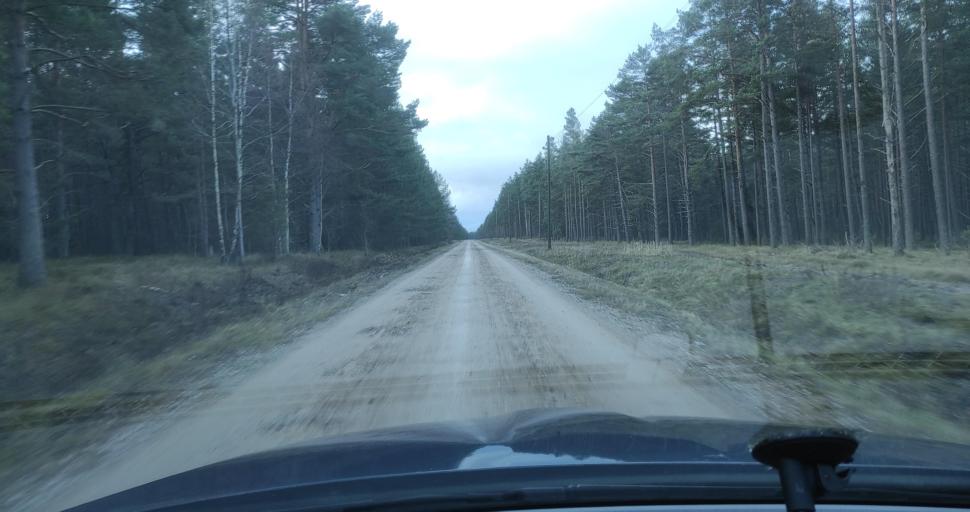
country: LV
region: Pavilostas
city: Pavilosta
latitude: 56.8118
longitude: 21.0654
